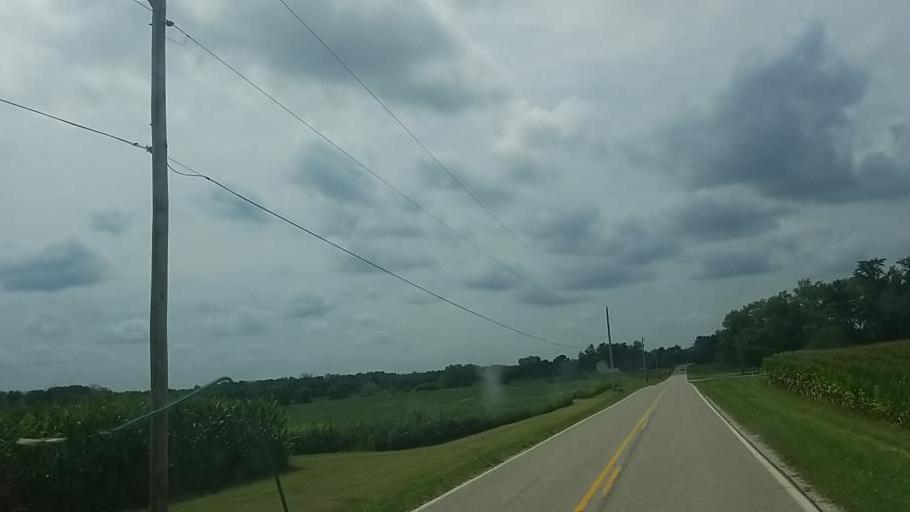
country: US
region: Ohio
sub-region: Fairfield County
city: Lithopolis
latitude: 39.7516
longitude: -82.8321
